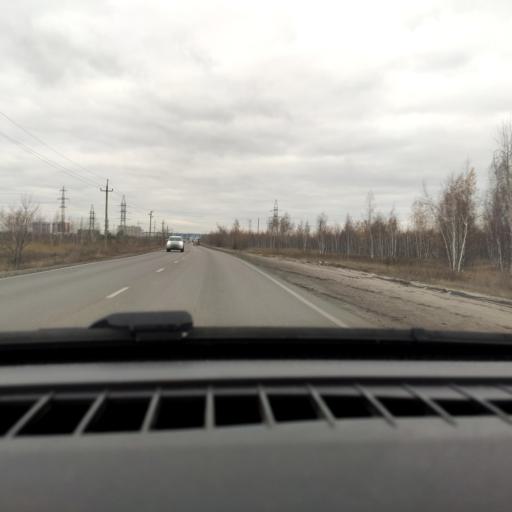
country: RU
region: Voronezj
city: Maslovka
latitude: 51.5785
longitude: 39.2653
